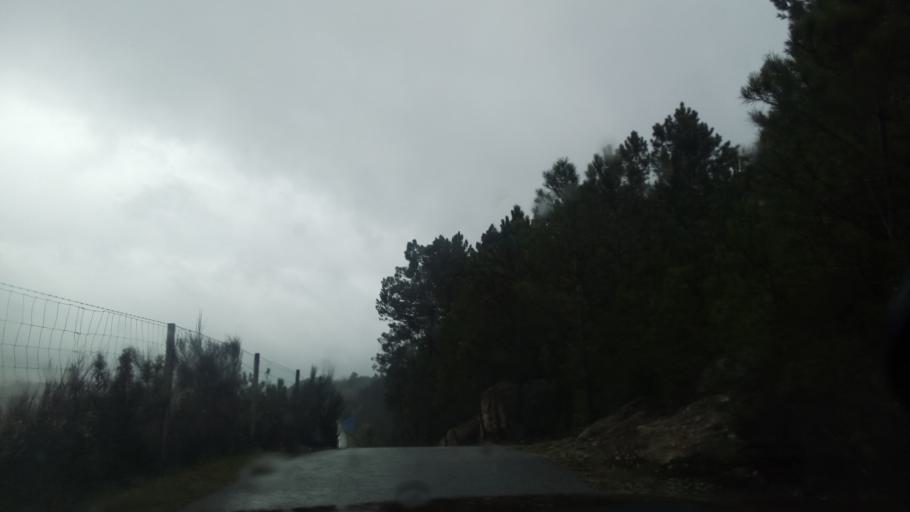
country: PT
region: Guarda
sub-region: Fornos de Algodres
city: Fornos de Algodres
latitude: 40.6181
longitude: -7.5214
